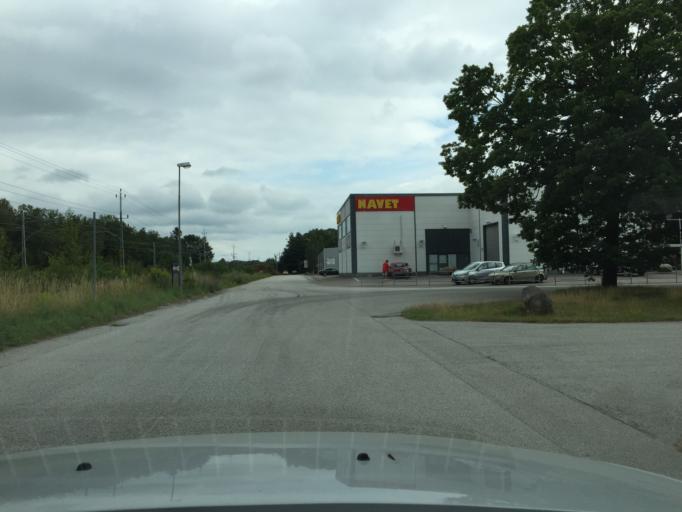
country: SE
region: Skane
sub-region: Hoors Kommun
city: Hoeoer
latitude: 55.9521
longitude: 13.5597
